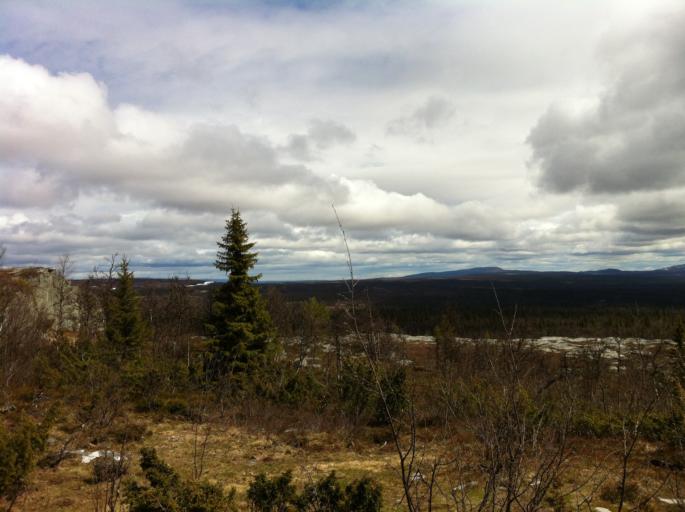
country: SE
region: Jaemtland
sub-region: Are Kommun
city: Are
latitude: 62.6849
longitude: 12.9676
